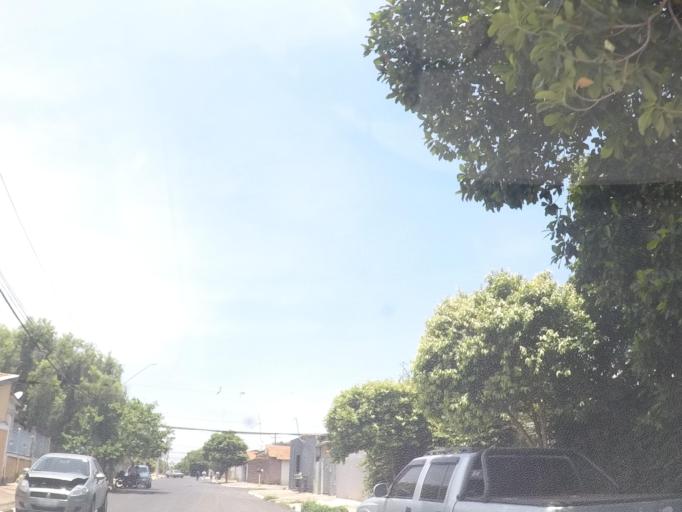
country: BR
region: Sao Paulo
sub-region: Hortolandia
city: Hortolandia
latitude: -22.8503
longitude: -47.1817
